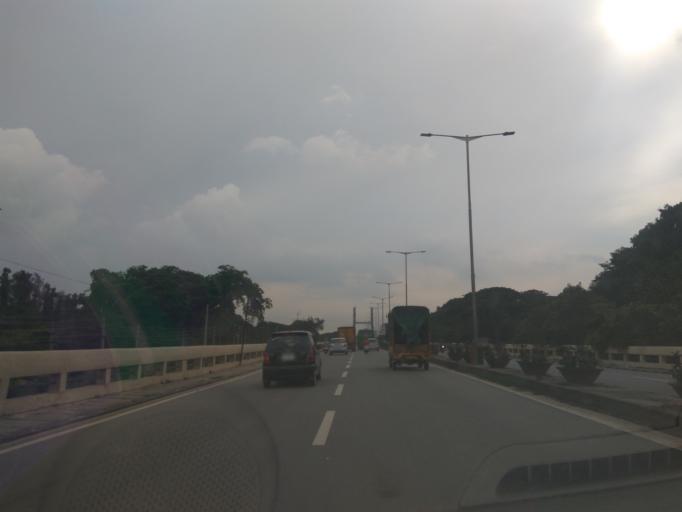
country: IN
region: Karnataka
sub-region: Bangalore Urban
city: Bangalore
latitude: 13.0042
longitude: 77.6835
